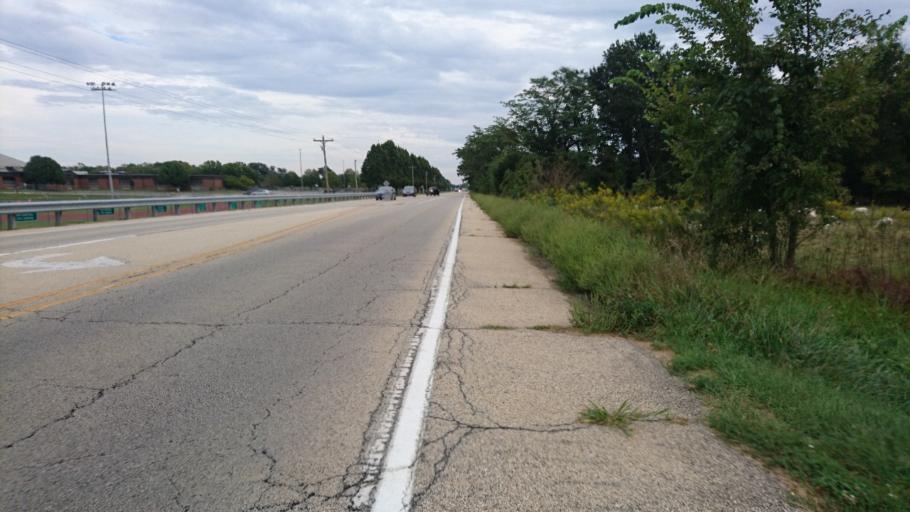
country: US
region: Illinois
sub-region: Sangamon County
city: Chatham
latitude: 39.6734
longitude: -89.6588
